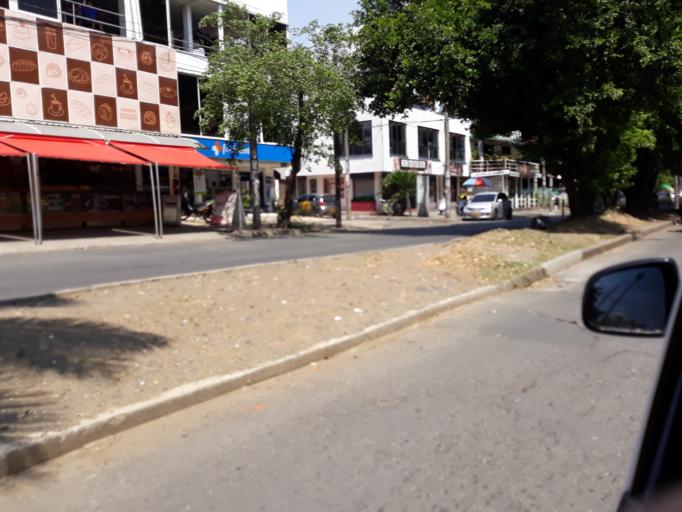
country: CO
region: Valle del Cauca
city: Cali
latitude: 3.4792
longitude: -76.4963
